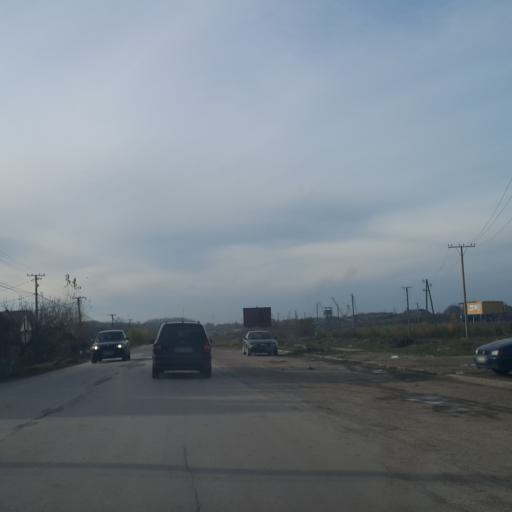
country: RS
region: Central Serbia
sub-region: Belgrade
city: Lazarevac
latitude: 44.3994
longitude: 20.3688
